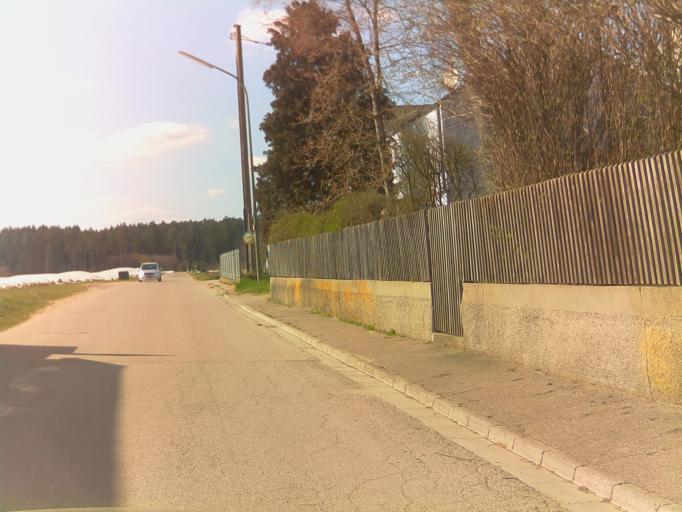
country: DE
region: Bavaria
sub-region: Swabia
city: Inchenhofen
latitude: 48.5510
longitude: 11.1180
